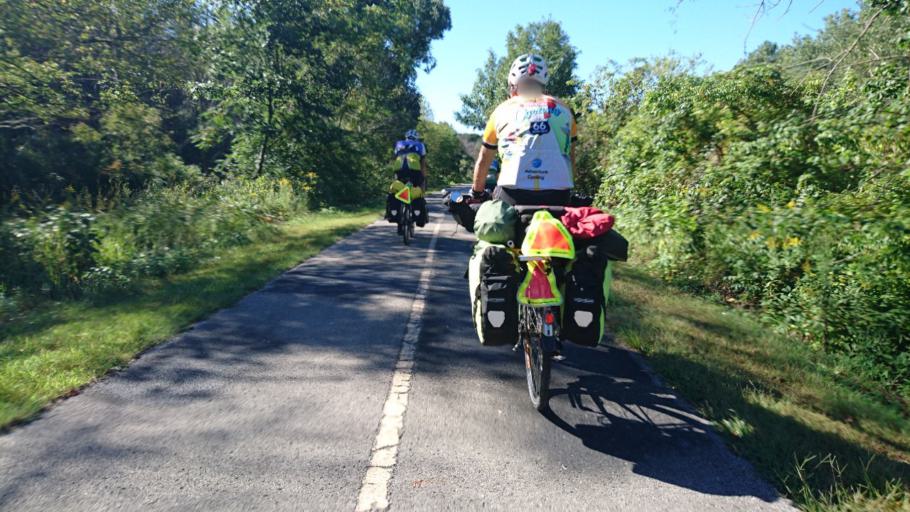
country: US
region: Indiana
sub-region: Lake County
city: Whiting
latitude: 41.6837
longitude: -87.5306
